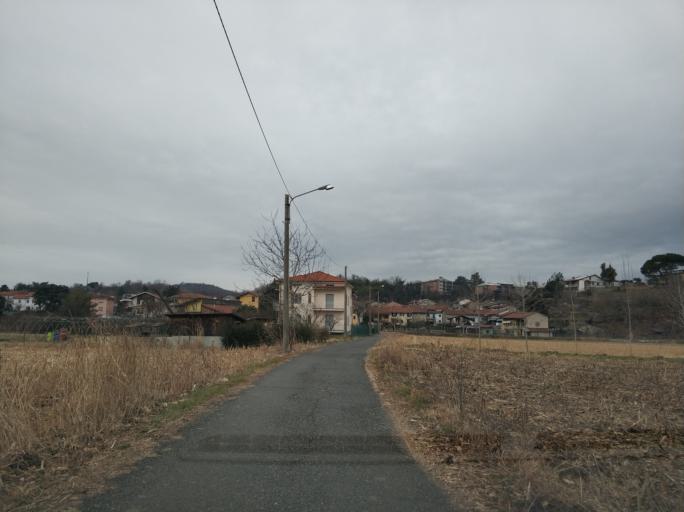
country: IT
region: Piedmont
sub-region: Provincia di Torino
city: Ivrea
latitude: 45.4446
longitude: 7.8822
